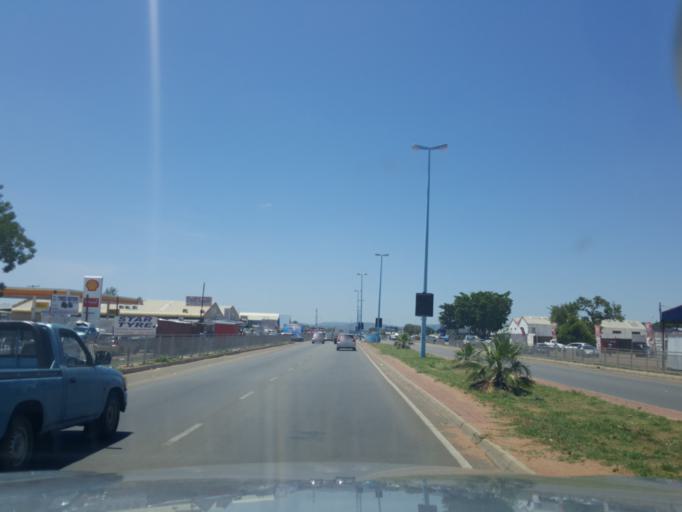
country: BW
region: Kweneng
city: Mogoditshane
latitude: -24.6158
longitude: 25.8634
